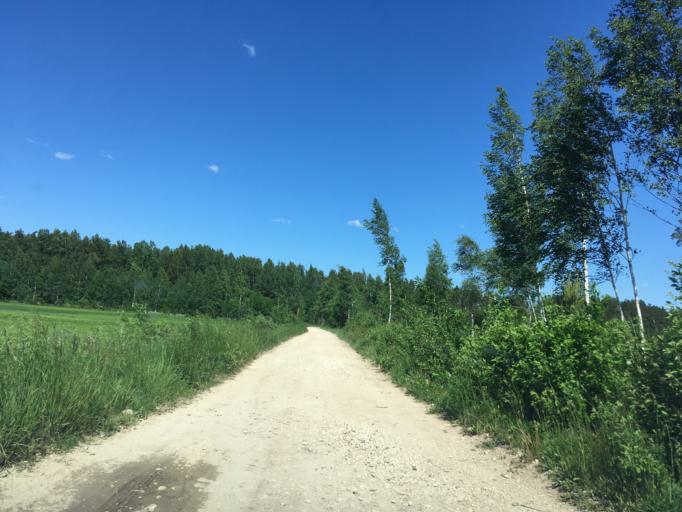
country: EE
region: Harju
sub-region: Raasiku vald
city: Raasiku
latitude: 59.1591
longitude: 25.1586
